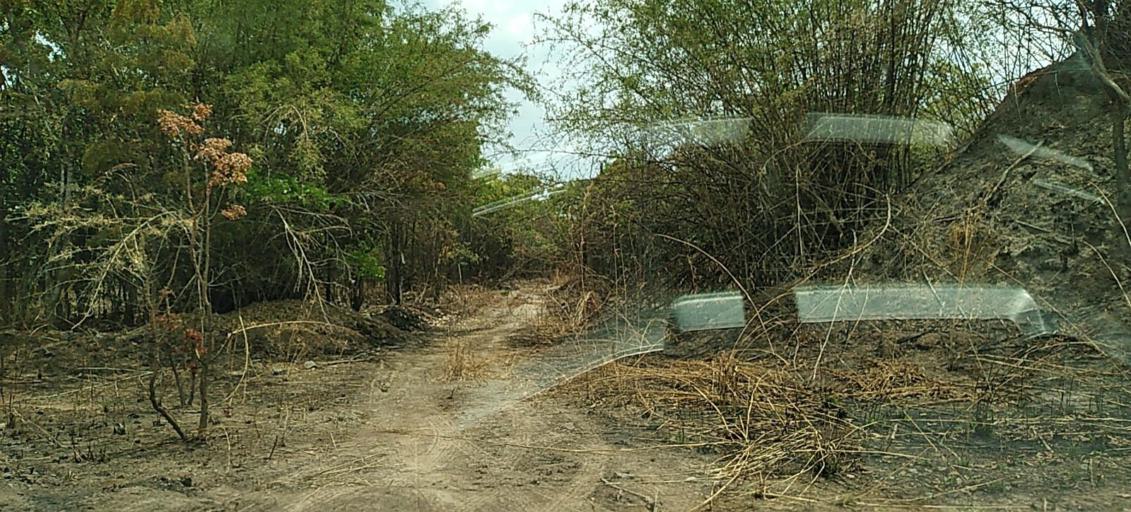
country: ZM
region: Copperbelt
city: Chililabombwe
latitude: -12.3302
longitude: 27.7679
